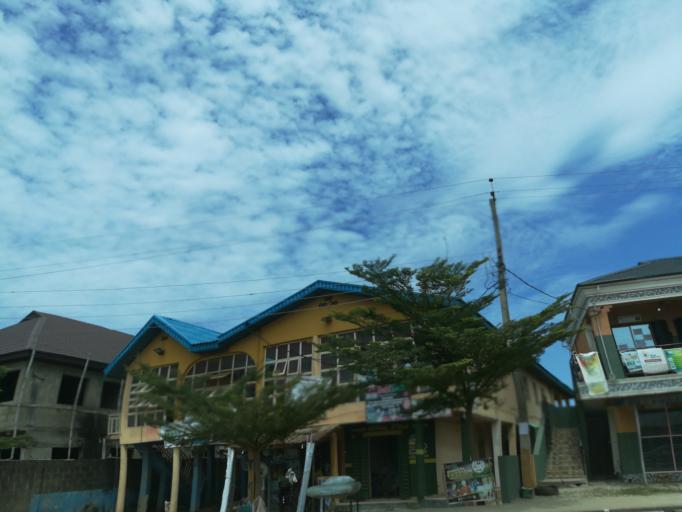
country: NG
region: Lagos
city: Ebute Ikorodu
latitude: 6.5593
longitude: 3.4756
